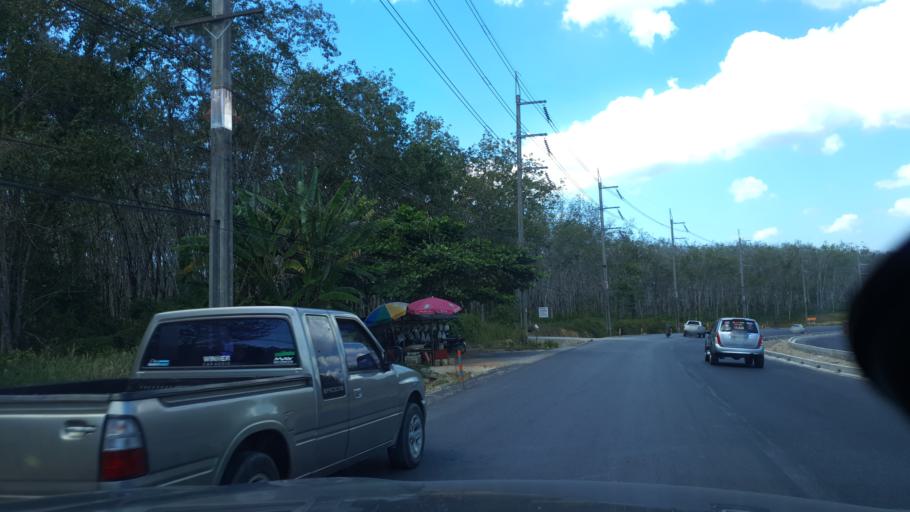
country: TH
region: Phangnga
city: Ban Khao Lak
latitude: 8.5466
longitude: 98.2705
